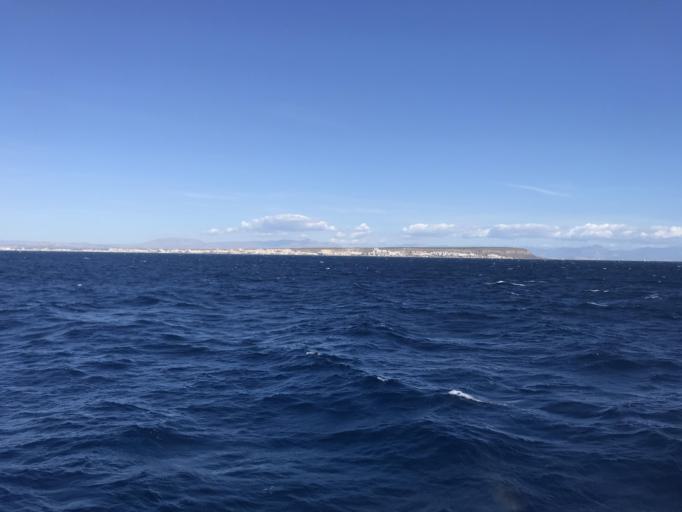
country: ES
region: Valencia
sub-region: Provincia de Alicante
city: Santa Pola
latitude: 38.1406
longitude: -0.5253
